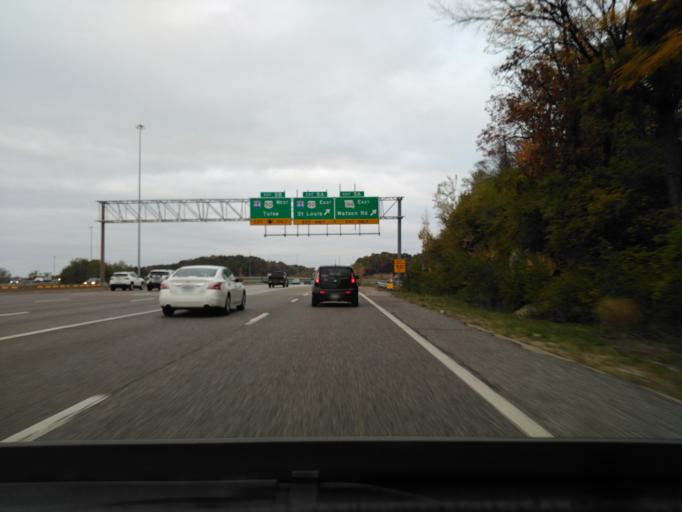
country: US
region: Missouri
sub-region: Saint Louis County
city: Sunset Hills
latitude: 38.5451
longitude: -90.4236
